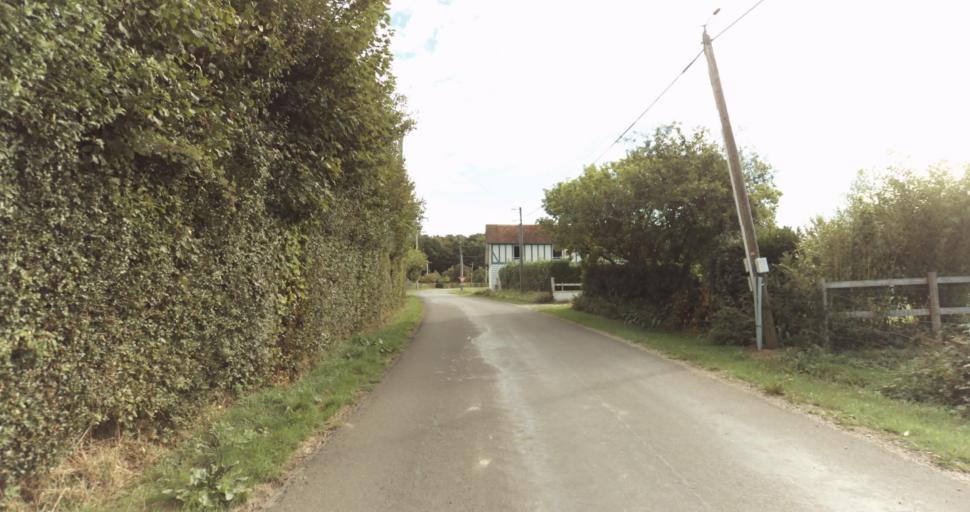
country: FR
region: Lower Normandy
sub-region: Departement de l'Orne
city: Gace
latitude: 48.8158
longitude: 0.2336
